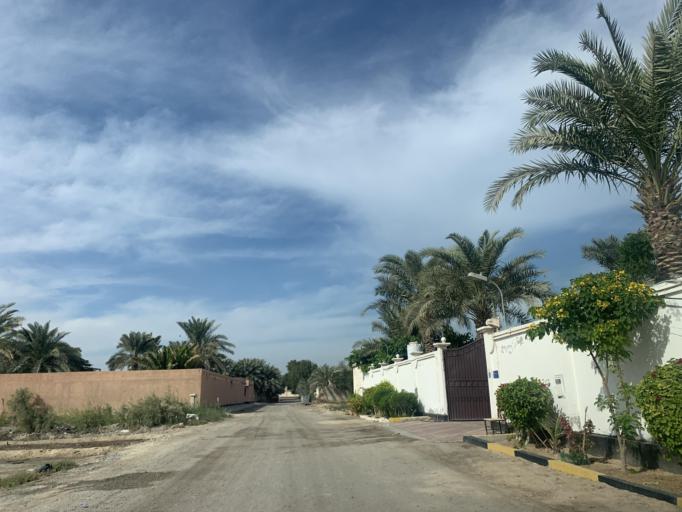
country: BH
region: Central Governorate
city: Madinat Hamad
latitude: 26.1213
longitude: 50.4682
